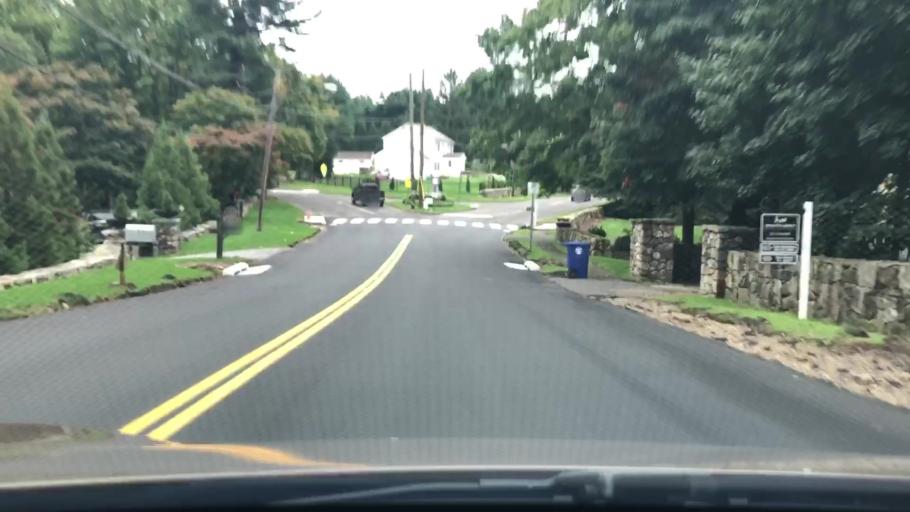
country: US
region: Connecticut
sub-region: Fairfield County
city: Norwalk
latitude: 41.1269
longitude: -73.4528
